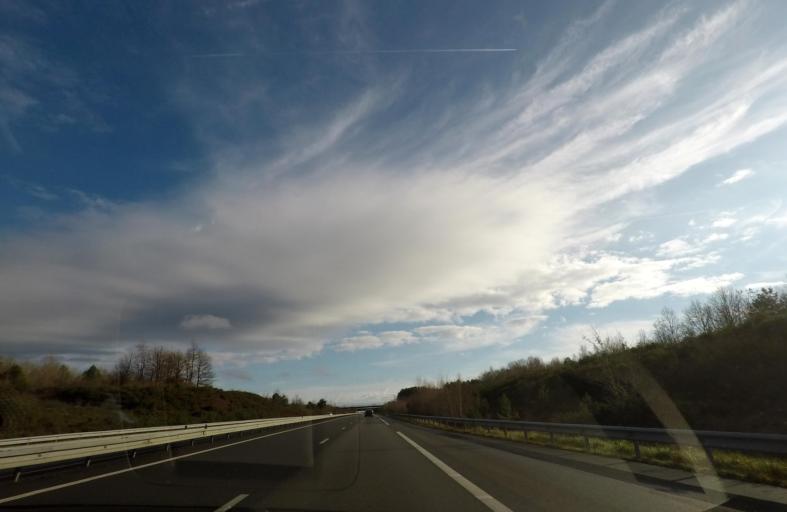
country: FR
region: Centre
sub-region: Departement du Loir-et-Cher
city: Villefranche-sur-Cher
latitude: 47.3126
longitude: 1.8222
